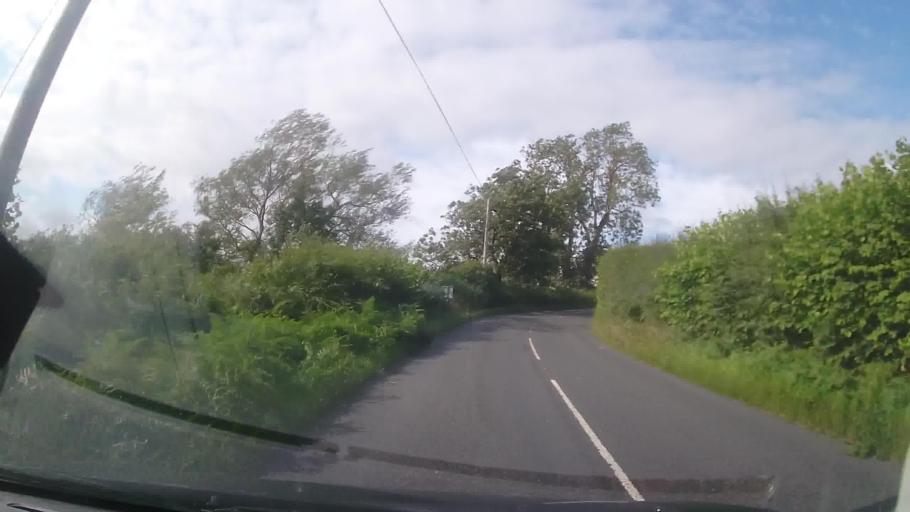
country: GB
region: England
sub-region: Shropshire
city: Acton
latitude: 52.4377
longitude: -3.0359
